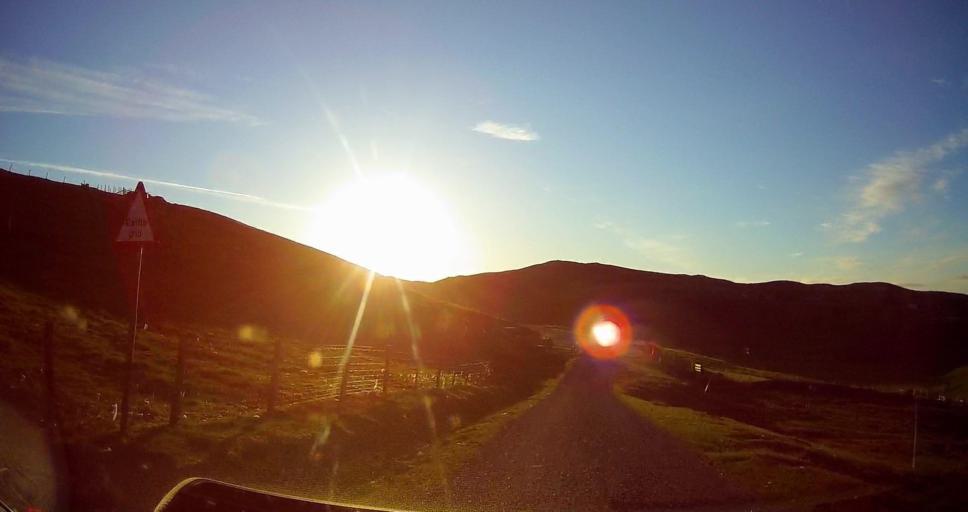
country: GB
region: Scotland
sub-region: Shetland Islands
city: Lerwick
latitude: 60.4477
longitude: -1.4155
